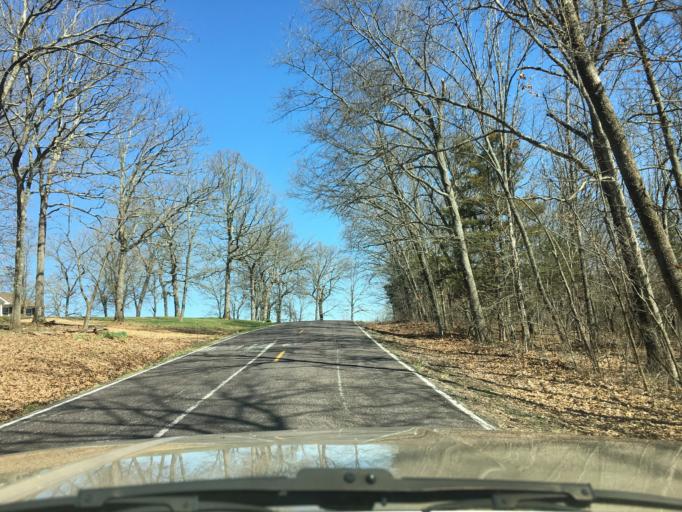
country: US
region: Missouri
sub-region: Franklin County
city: Gerald
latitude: 38.5325
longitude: -91.3328
